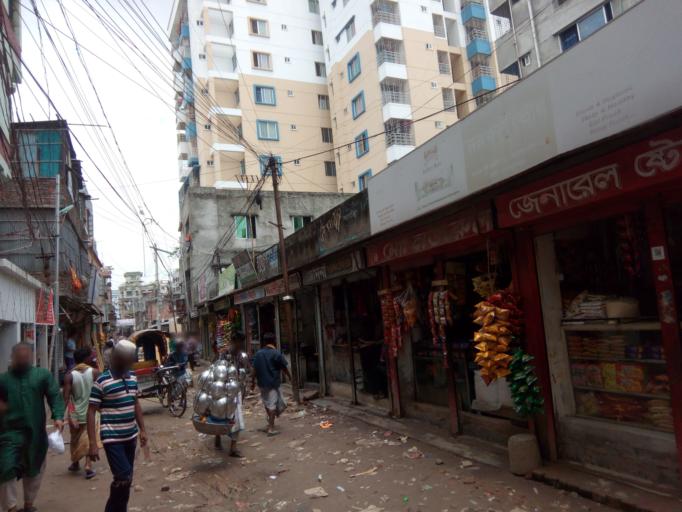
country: BD
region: Dhaka
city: Azimpur
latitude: 23.7505
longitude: 90.3596
